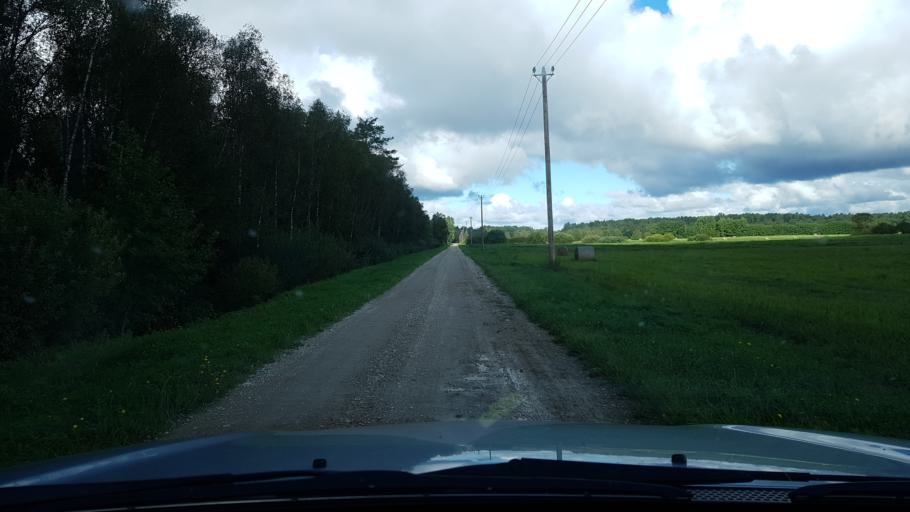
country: EE
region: Harju
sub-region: Rae vald
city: Vaida
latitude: 59.2494
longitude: 25.0714
